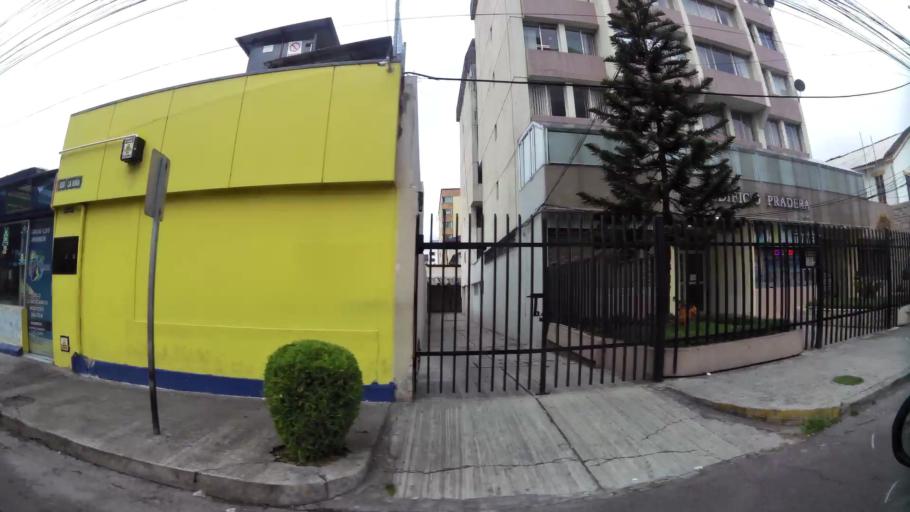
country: EC
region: Pichincha
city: Quito
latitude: -0.1981
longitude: -78.4894
